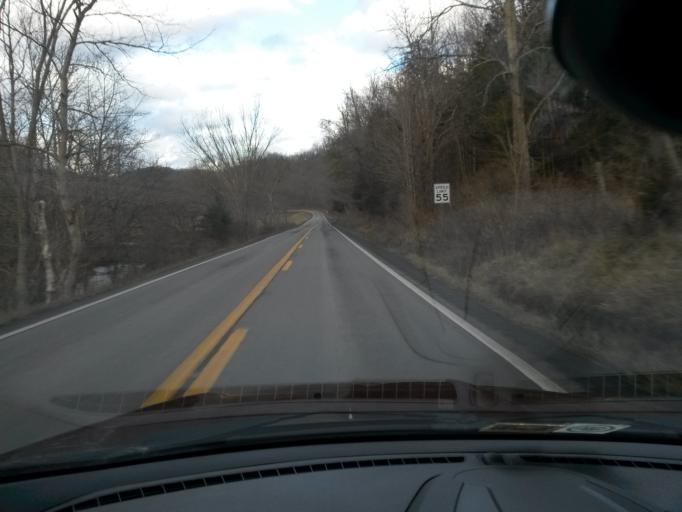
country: US
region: West Virginia
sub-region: Monroe County
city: Union
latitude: 37.5482
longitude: -80.5743
